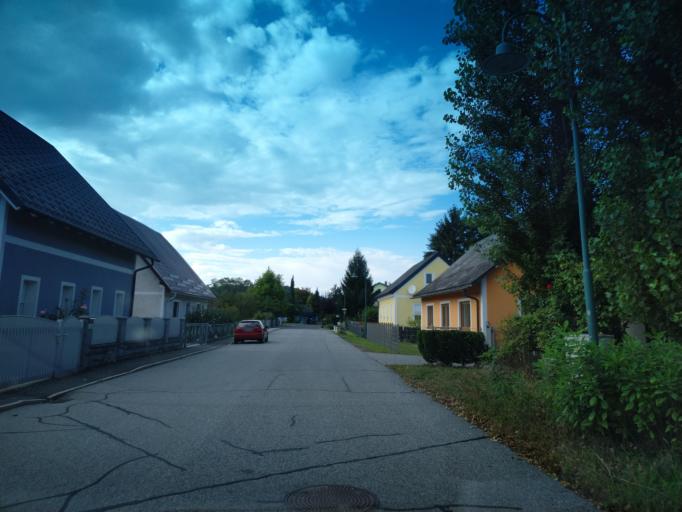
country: AT
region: Styria
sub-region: Politischer Bezirk Leibnitz
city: Kaindorf an der Sulm
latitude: 46.7892
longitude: 15.5365
